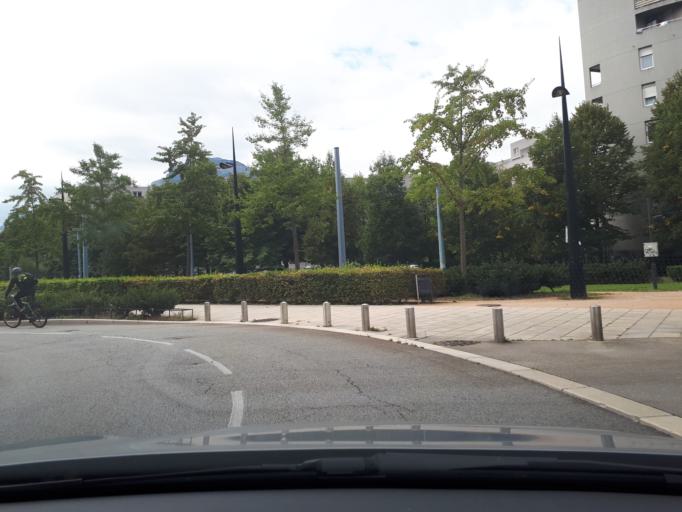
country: FR
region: Rhone-Alpes
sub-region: Departement de l'Isere
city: Saint-Martin-le-Vinoux
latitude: 45.1935
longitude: 5.7112
